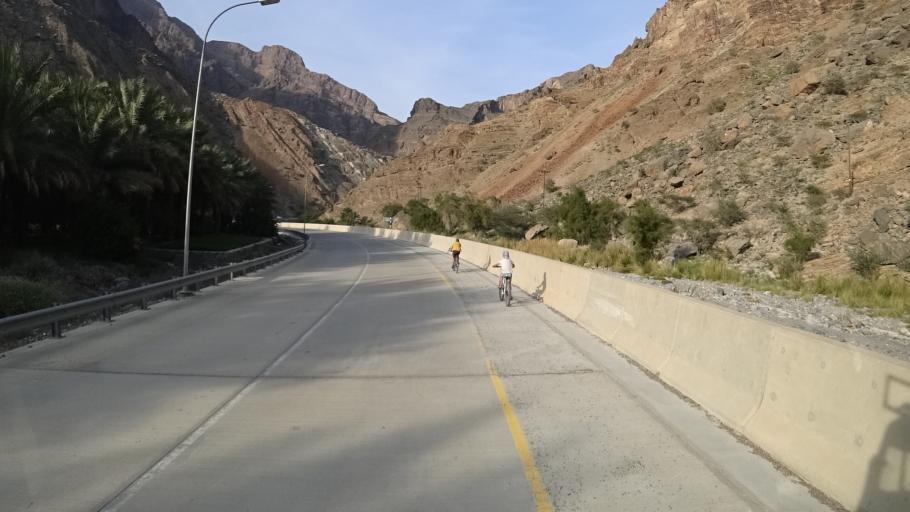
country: OM
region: Al Batinah
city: Bayt al `Awabi
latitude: 23.2826
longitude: 57.4657
